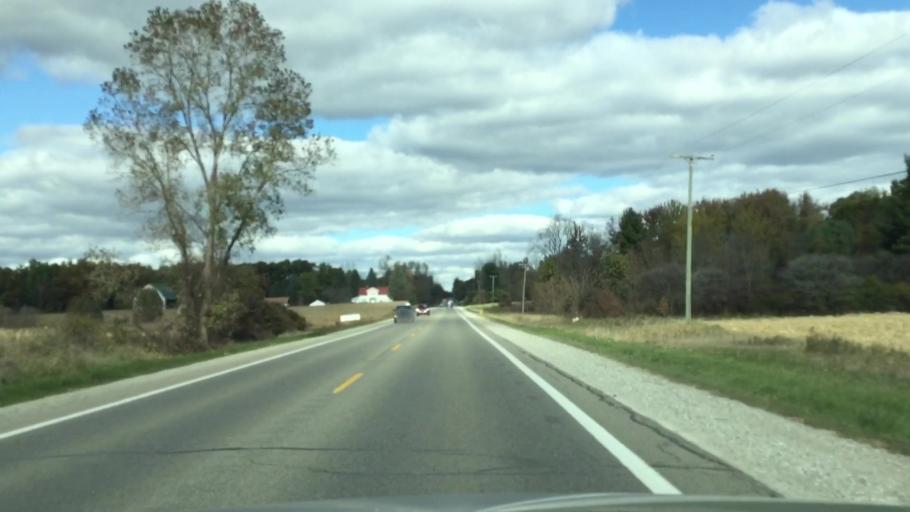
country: US
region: Michigan
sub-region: Lapeer County
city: Barnes Lake-Millers Lake
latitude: 43.1228
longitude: -83.3097
